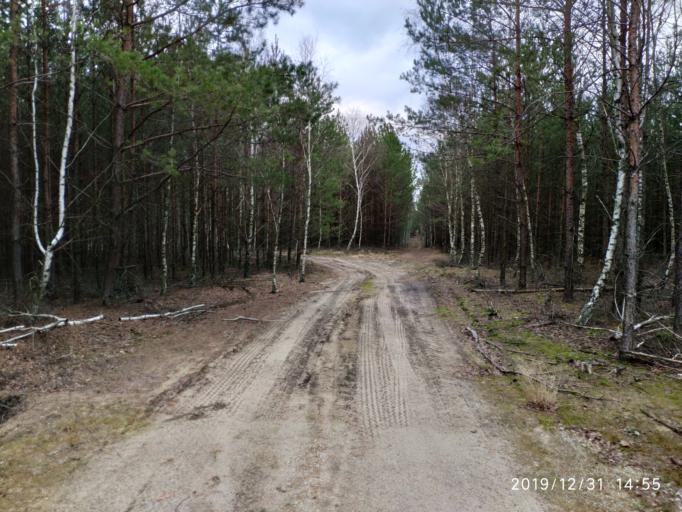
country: PL
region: Lubusz
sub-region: Powiat zielonogorski
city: Czerwiensk
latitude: 52.0068
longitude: 15.3878
